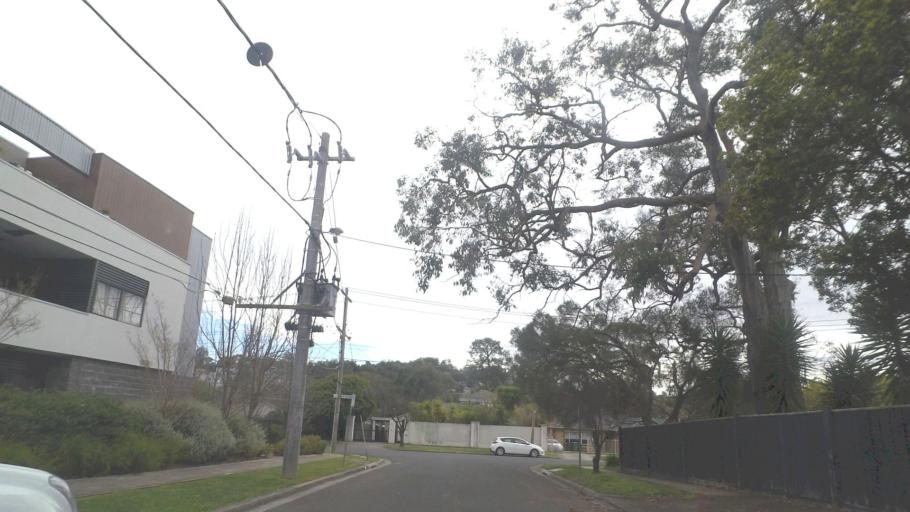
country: AU
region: Victoria
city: Mitcham
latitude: -37.8119
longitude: 145.2230
